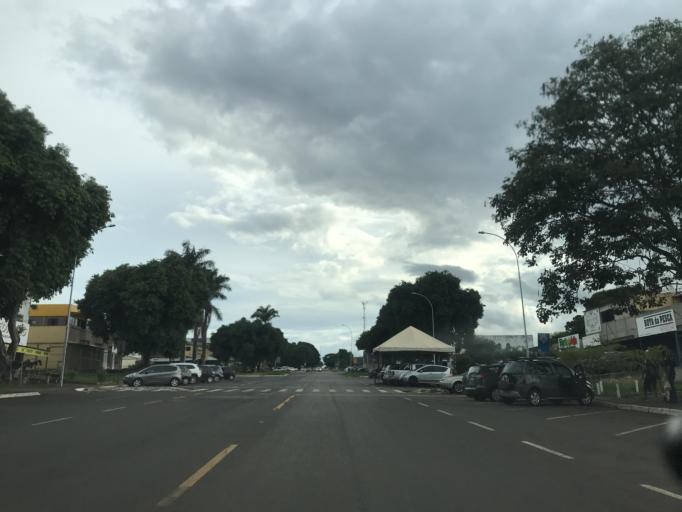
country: BR
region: Federal District
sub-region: Brasilia
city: Brasilia
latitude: -15.6418
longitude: -47.7926
